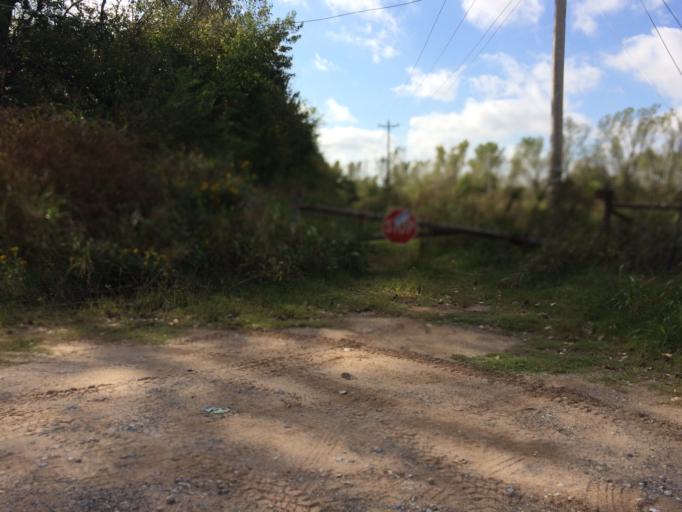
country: US
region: Oklahoma
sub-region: McClain County
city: Goldsby
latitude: 35.1903
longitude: -97.4768
